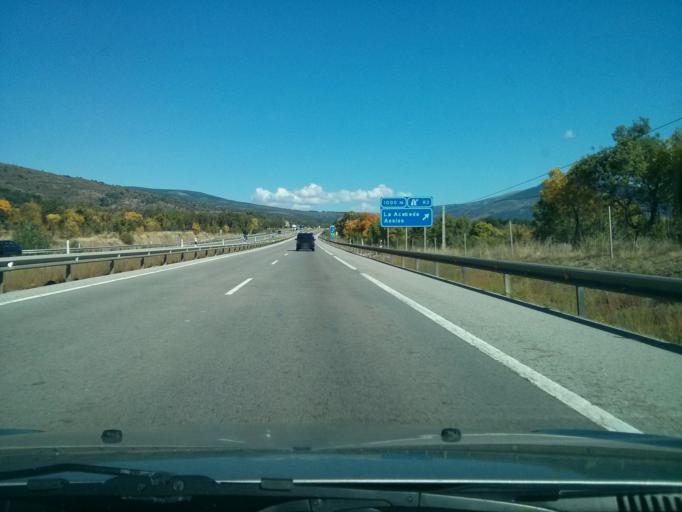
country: ES
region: Madrid
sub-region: Provincia de Madrid
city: Braojos
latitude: 41.0486
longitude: -3.6155
